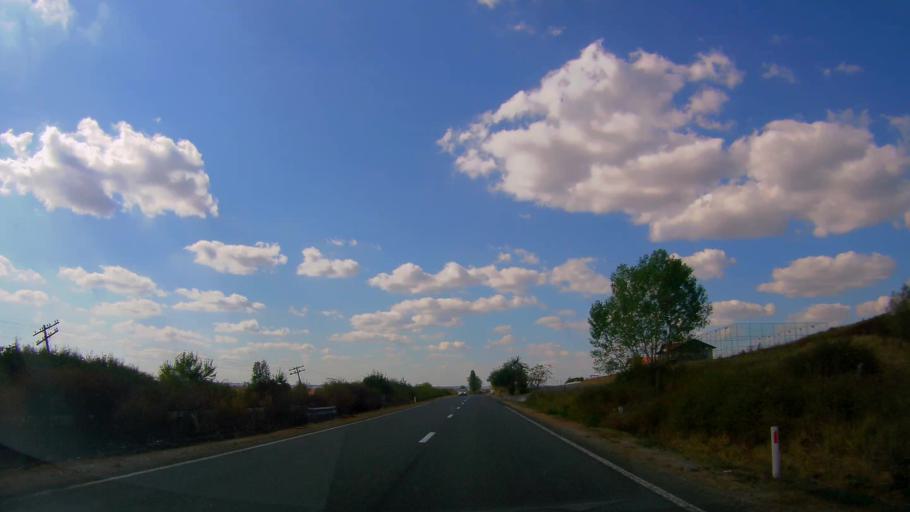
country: RO
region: Salaj
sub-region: Comuna Sarmasag
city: Sarmasag
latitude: 47.3300
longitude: 22.8616
